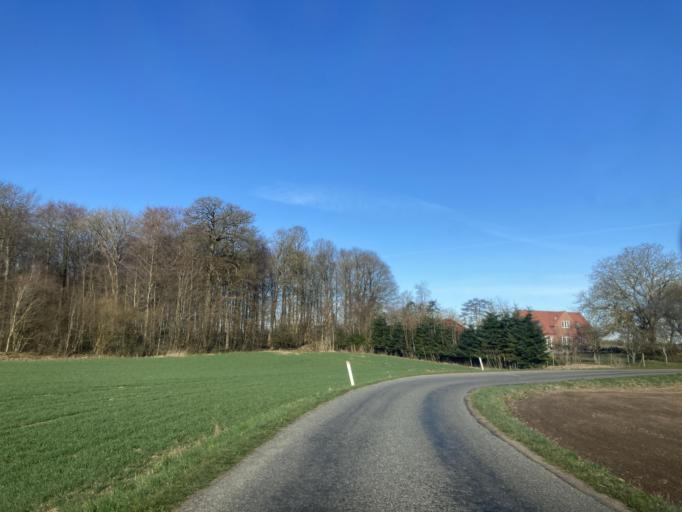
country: DK
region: Zealand
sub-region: Lejre Kommune
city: Kirke Hvalso
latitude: 55.5037
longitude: 11.8547
